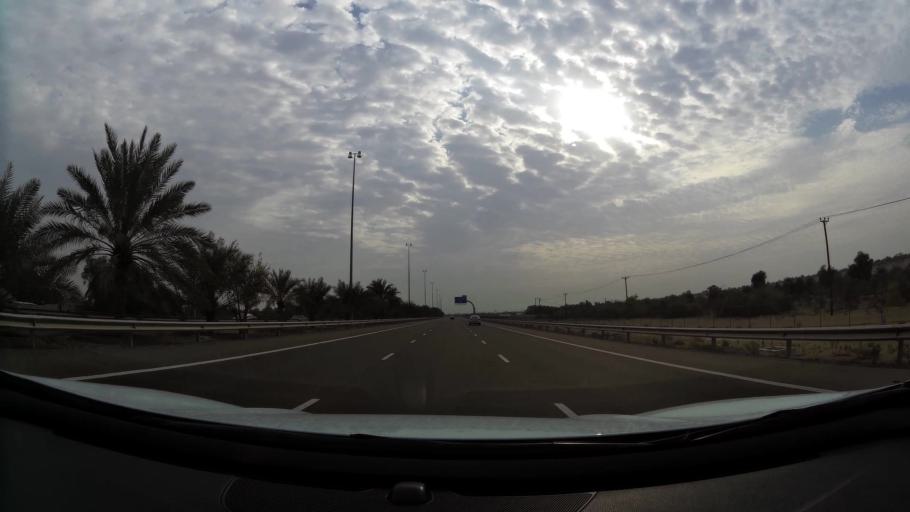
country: AE
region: Abu Dhabi
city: Al Ain
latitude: 24.1688
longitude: 55.0829
